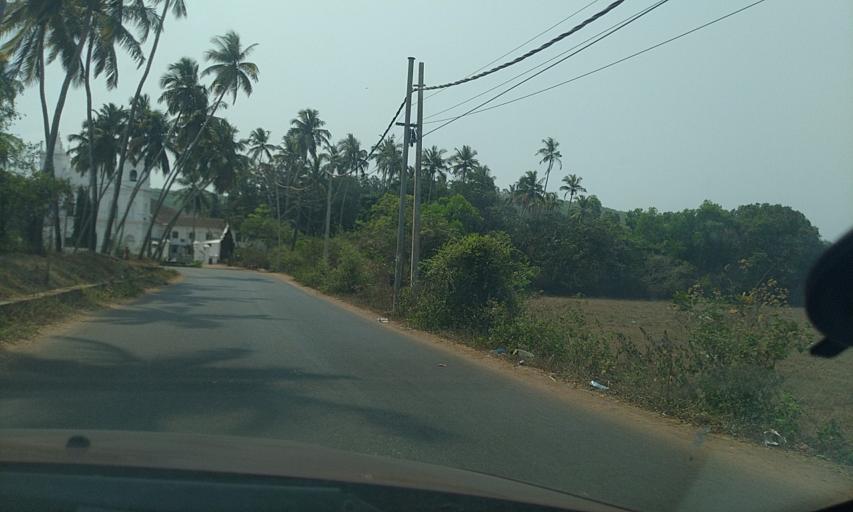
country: IN
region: Goa
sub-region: North Goa
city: Vagator
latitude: 15.5912
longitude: 73.7636
